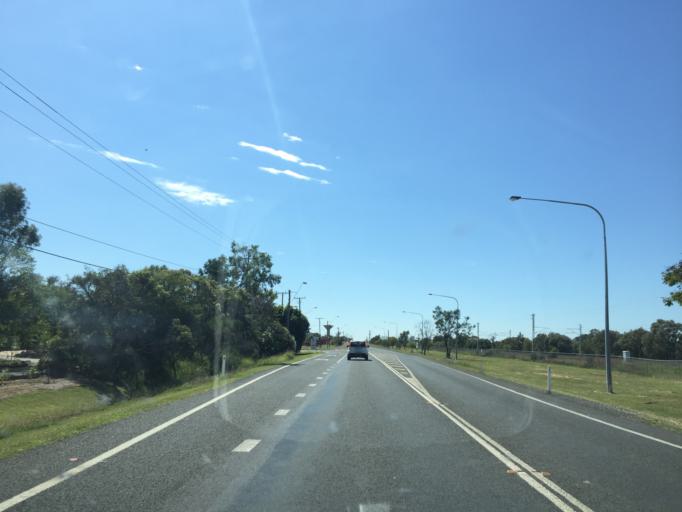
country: AU
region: Queensland
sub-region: Central Highlands
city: Blackwater
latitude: -23.5858
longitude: 148.8712
